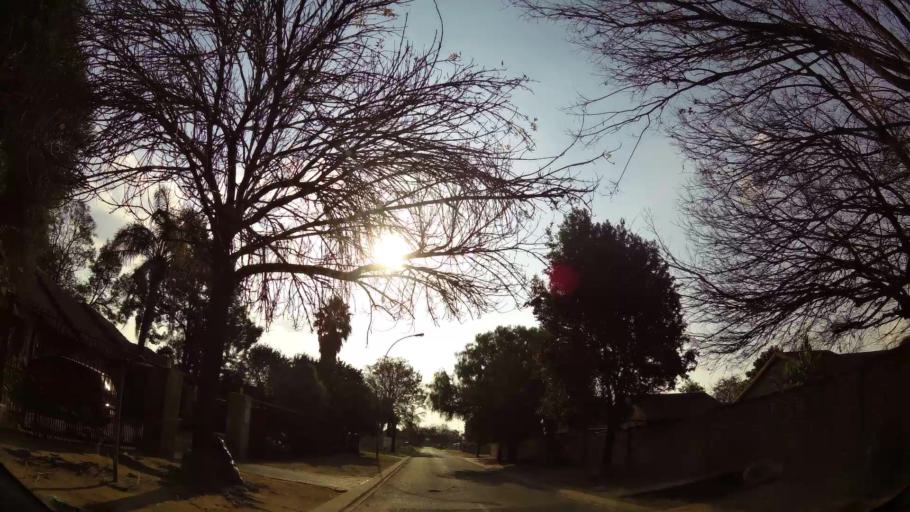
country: ZA
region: Gauteng
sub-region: Ekurhuleni Metropolitan Municipality
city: Benoni
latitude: -26.1296
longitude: 28.3673
